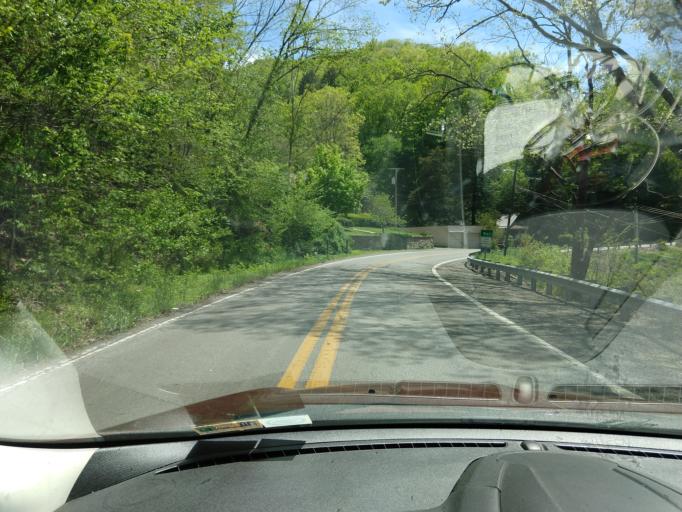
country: US
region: West Virginia
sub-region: McDowell County
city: Welch
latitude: 37.3125
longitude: -81.6940
